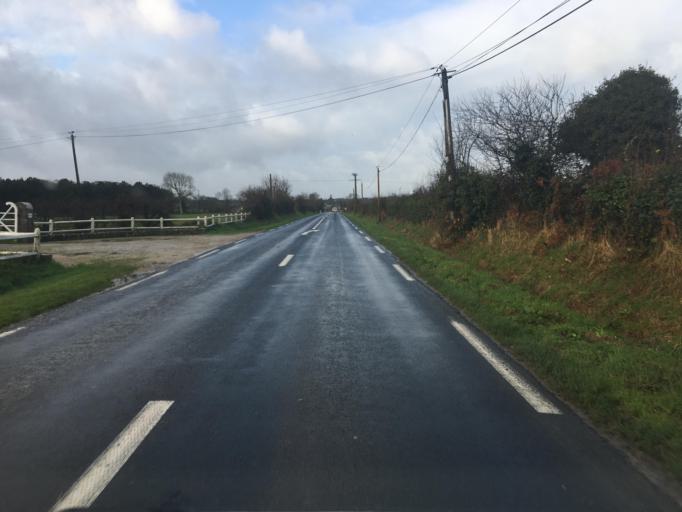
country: FR
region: Lower Normandy
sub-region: Departement de la Manche
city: Saint-Pierre-Eglise
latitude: 49.6706
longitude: -1.3277
